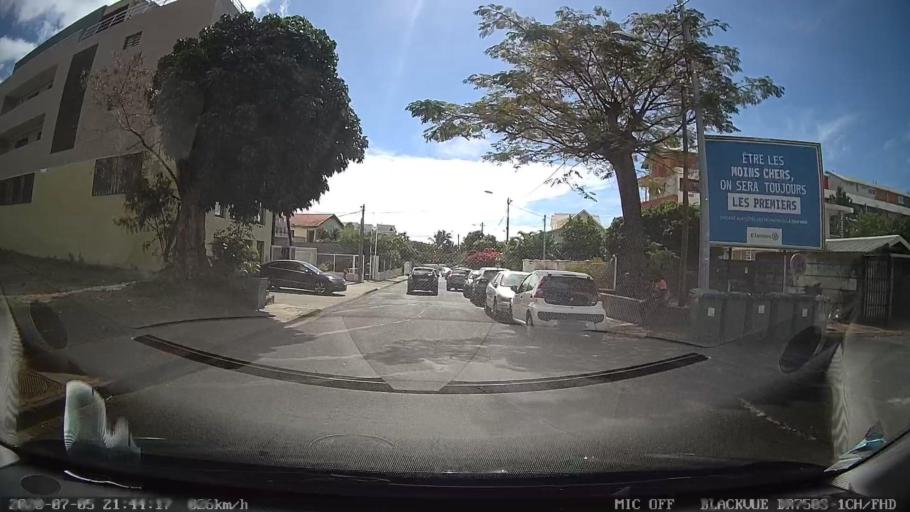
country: RE
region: Reunion
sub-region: Reunion
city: Saint-Denis
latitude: -20.8874
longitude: 55.4795
